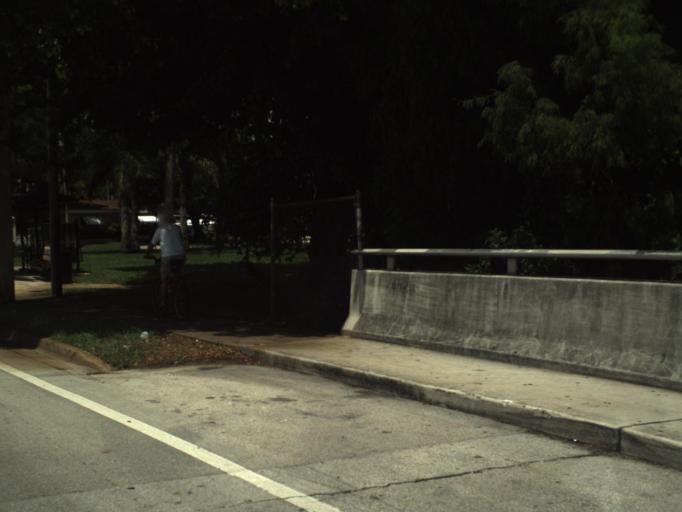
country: US
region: Florida
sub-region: Broward County
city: Hollywood
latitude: 26.0110
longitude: -80.1684
